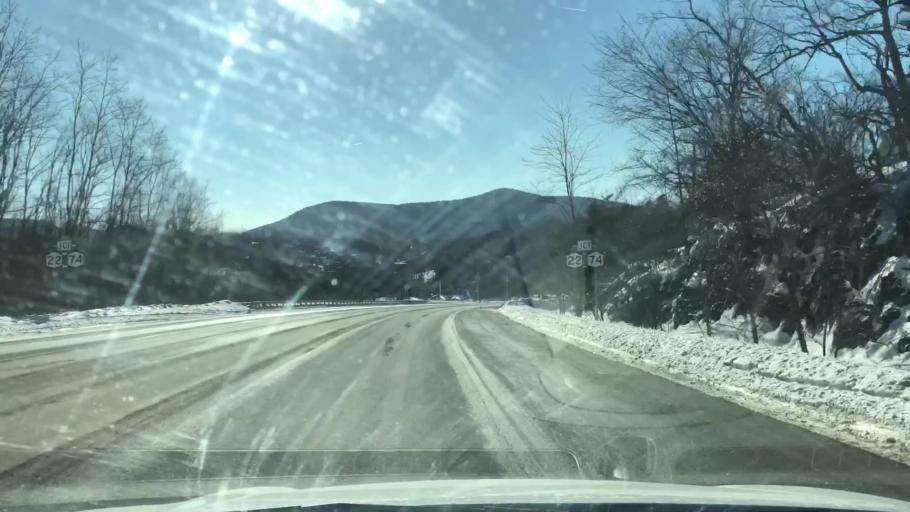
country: US
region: New York
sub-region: Essex County
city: Ticonderoga
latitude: 43.8585
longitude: -73.4139
